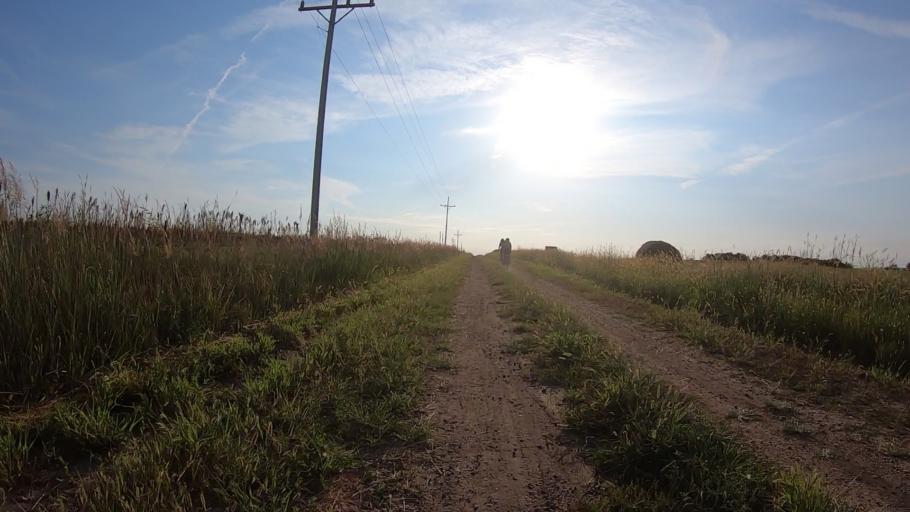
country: US
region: Kansas
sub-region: Marshall County
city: Blue Rapids
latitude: 39.7114
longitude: -96.8018
